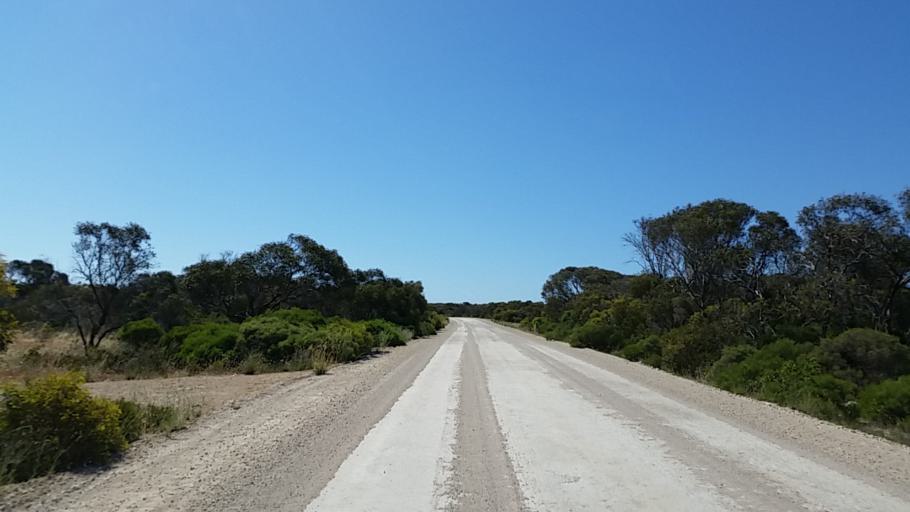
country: AU
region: South Australia
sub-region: Yorke Peninsula
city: Honiton
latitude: -35.2243
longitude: 137.1028
